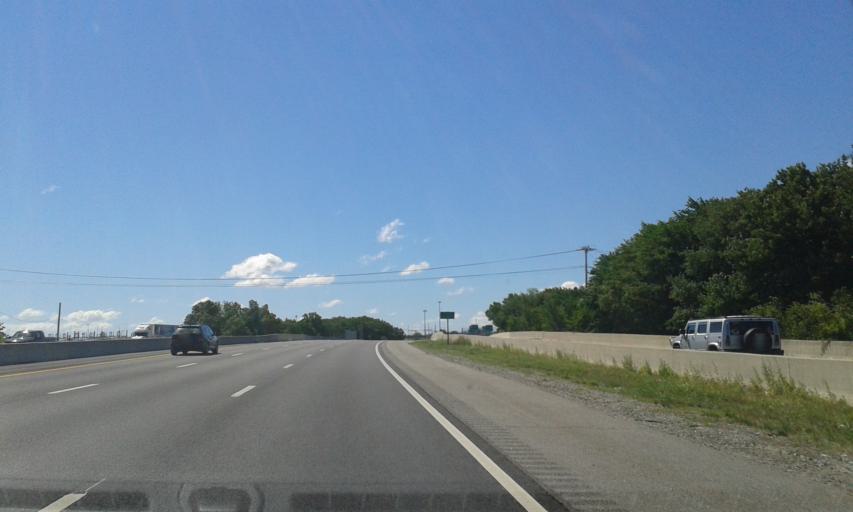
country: US
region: Massachusetts
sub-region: Middlesex County
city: Lowell
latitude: 42.6150
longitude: -71.3300
